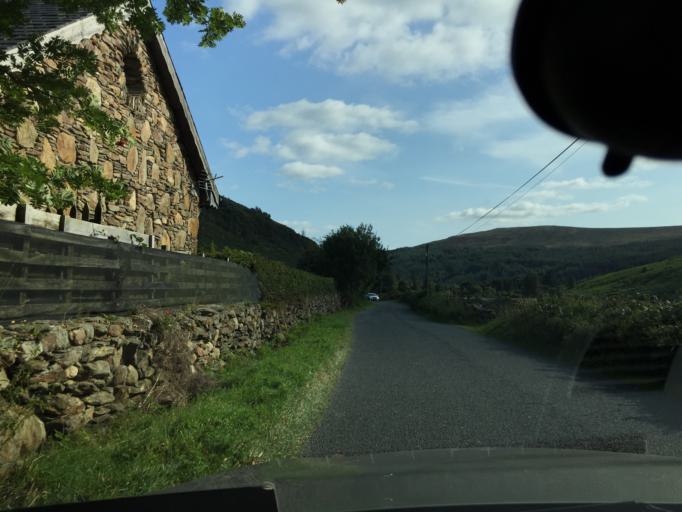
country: IE
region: Leinster
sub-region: Wicklow
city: Rathdrum
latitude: 53.0471
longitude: -6.3284
